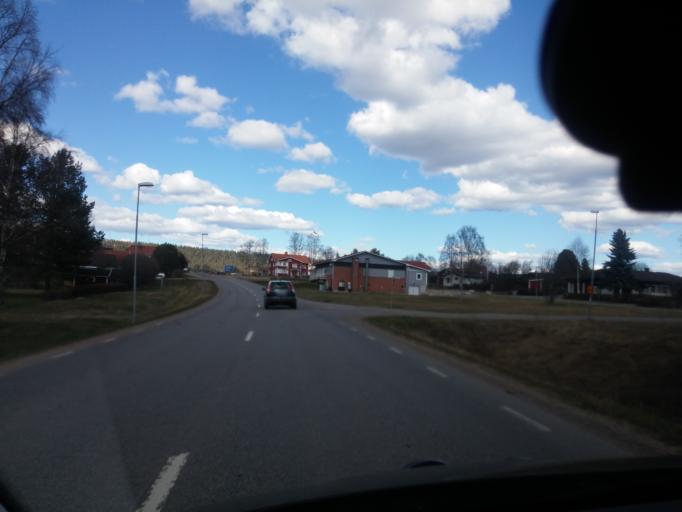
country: SE
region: Gaevleborg
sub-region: Ljusdals Kommun
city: Farila
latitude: 61.7958
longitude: 15.8364
